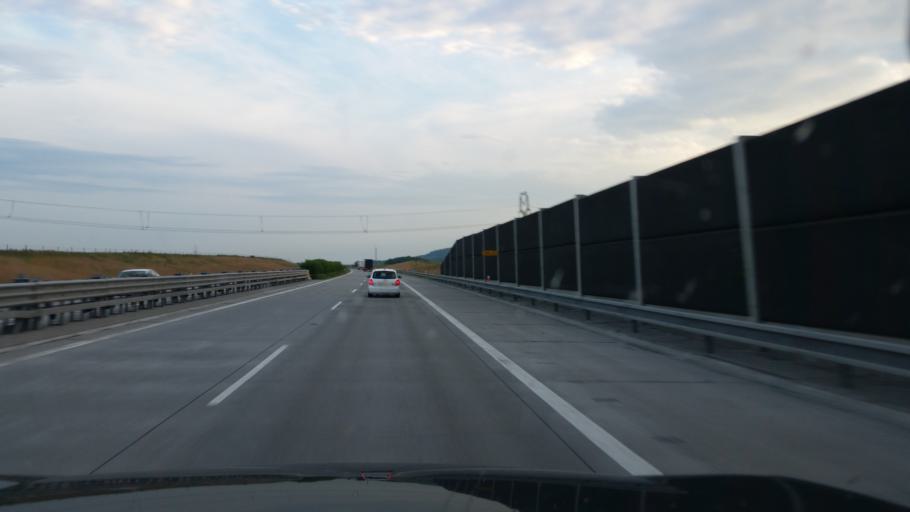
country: CZ
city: Fulnek
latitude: 49.6832
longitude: 17.9407
